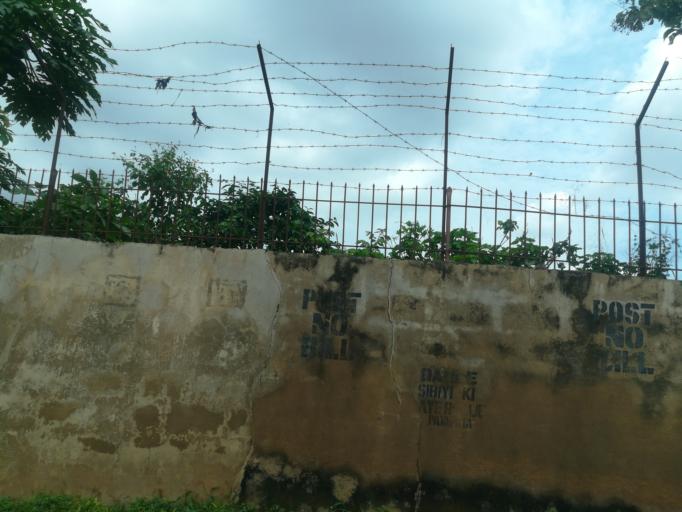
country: NG
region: Oyo
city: Ibadan
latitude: 7.4200
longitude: 3.9314
